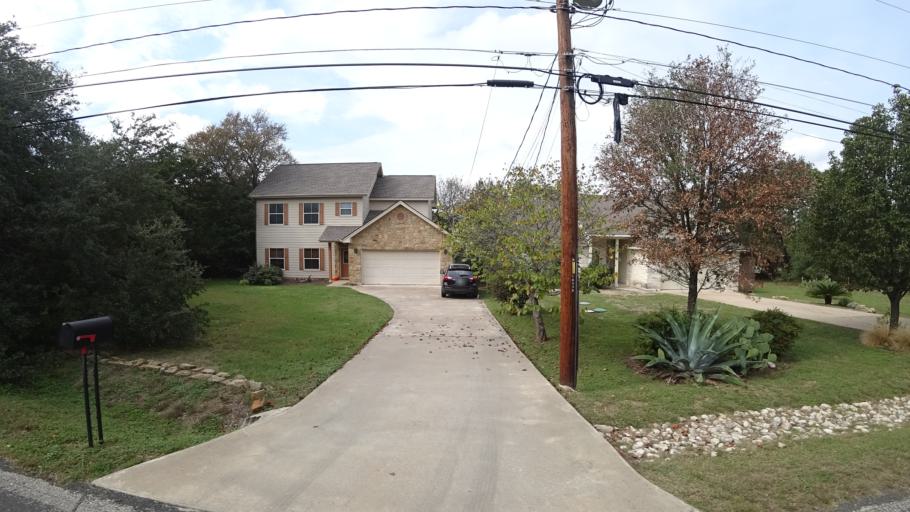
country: US
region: Texas
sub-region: Travis County
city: Hudson Bend
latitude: 30.3772
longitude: -97.9272
